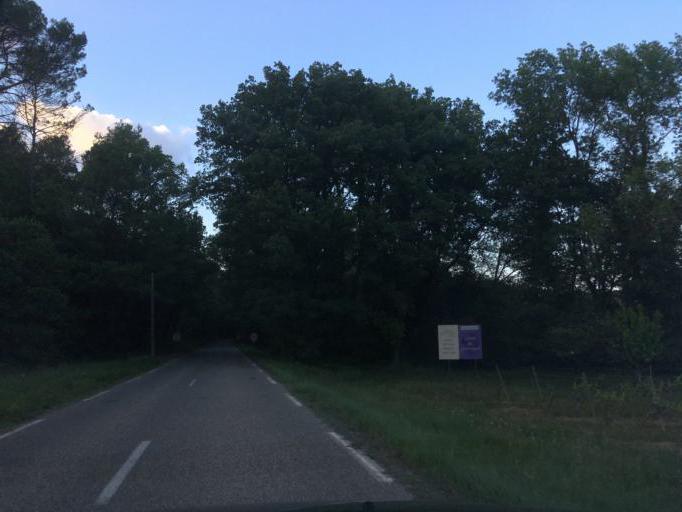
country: FR
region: Provence-Alpes-Cote d'Azur
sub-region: Departement du Var
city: Carces
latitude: 43.4975
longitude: 6.2224
